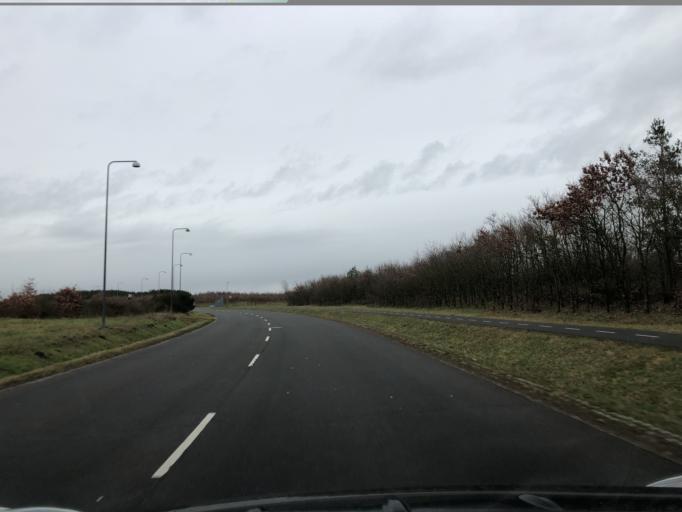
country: DK
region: Central Jutland
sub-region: Holstebro Kommune
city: Holstebro
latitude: 56.3604
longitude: 8.6647
